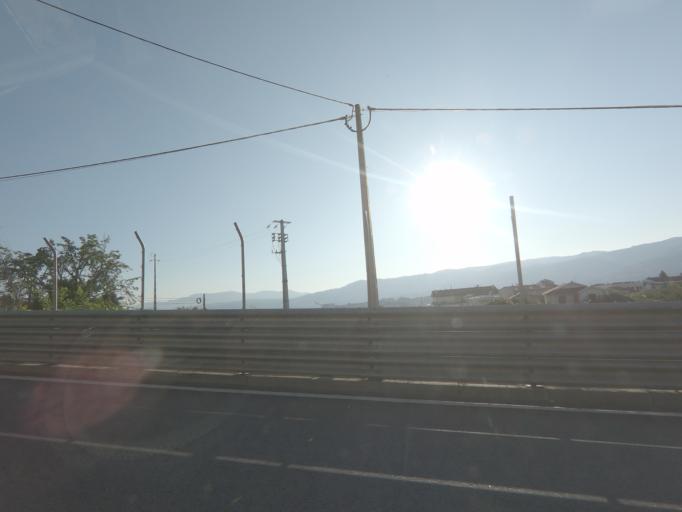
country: PT
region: Vila Real
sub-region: Vila Real
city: Vila Real
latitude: 41.3031
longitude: -7.7191
